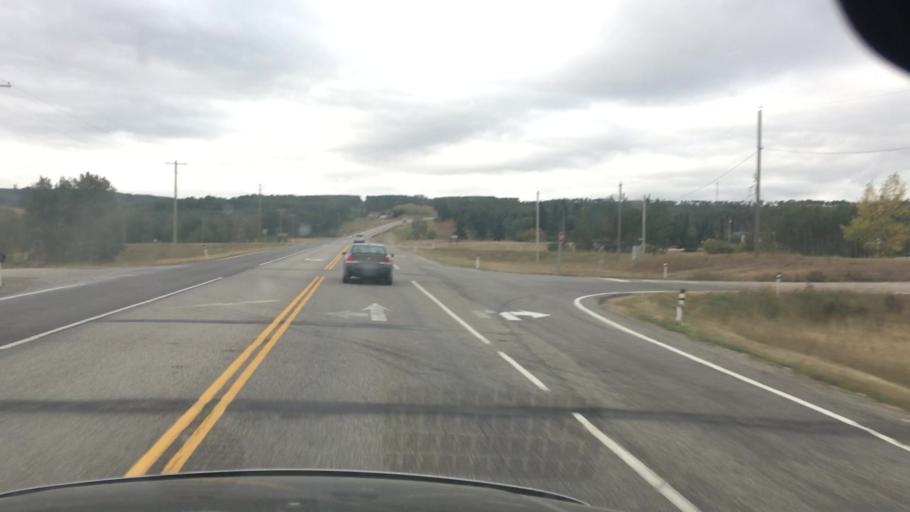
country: CA
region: Alberta
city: Cochrane
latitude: 51.3744
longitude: -114.4702
